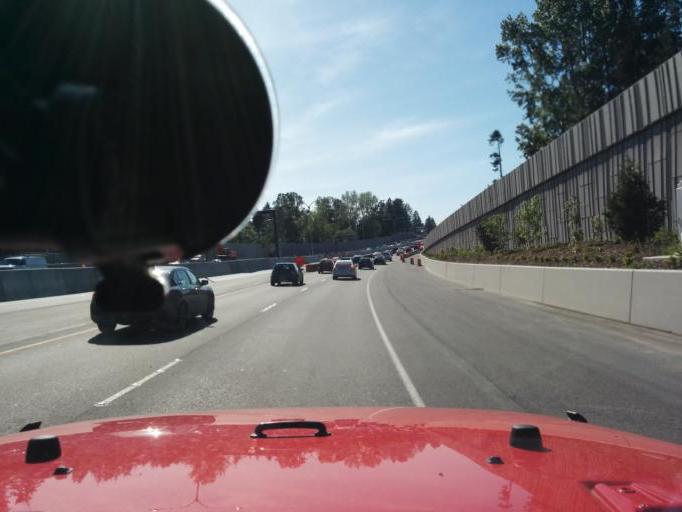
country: US
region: Washington
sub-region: King County
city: Clyde Hill
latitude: 47.6360
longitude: -122.2288
